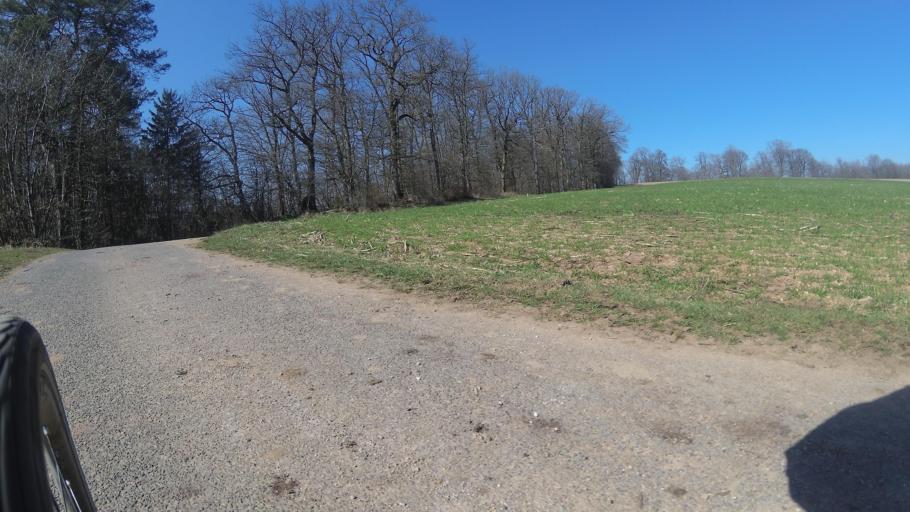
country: DE
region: Rheinland-Pfalz
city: Dambach
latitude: 49.6324
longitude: 7.1275
